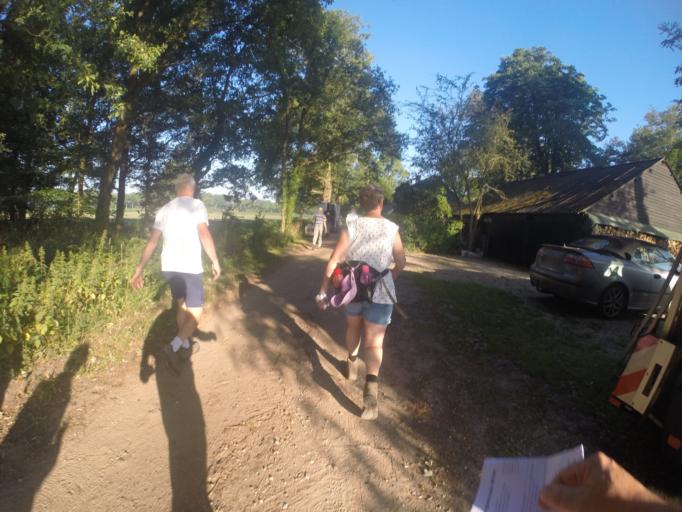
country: NL
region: Gelderland
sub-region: Gemeente Lochem
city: Lochem
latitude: 52.1208
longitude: 6.4008
